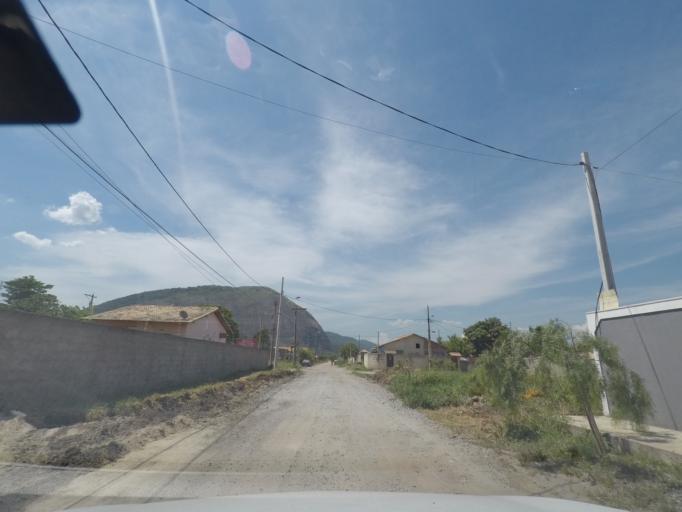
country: BR
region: Rio de Janeiro
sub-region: Marica
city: Marica
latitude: -22.9548
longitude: -42.9577
